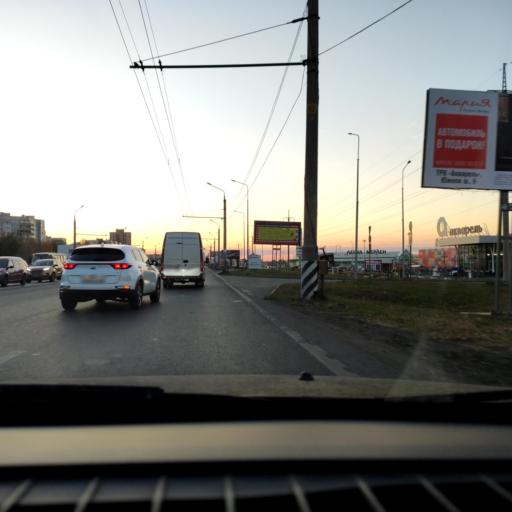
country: RU
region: Samara
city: Tol'yatti
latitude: 53.5482
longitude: 49.3467
